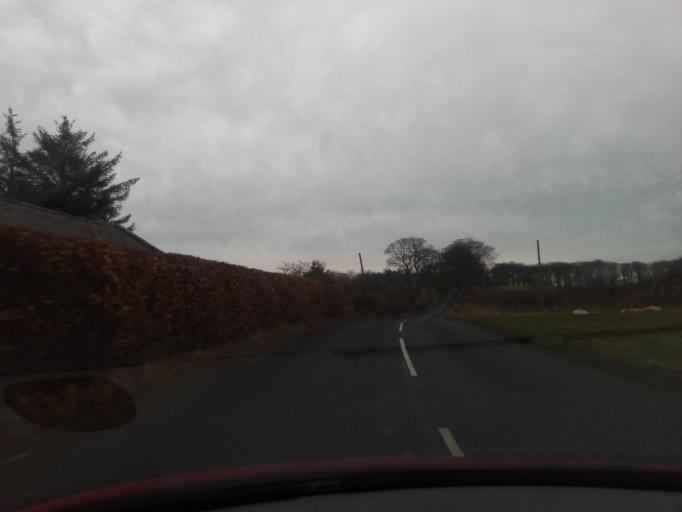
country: GB
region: England
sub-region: Northumberland
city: Whittingham
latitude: 55.4719
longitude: -1.8495
